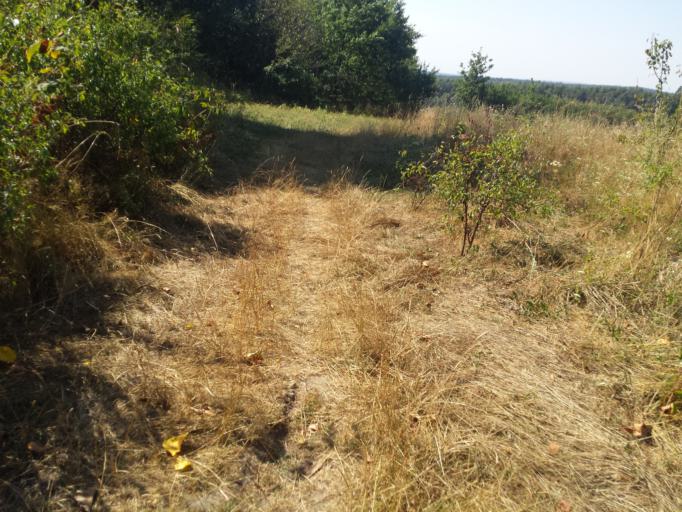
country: PL
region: Swietokrzyskie
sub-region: Powiat kielecki
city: Daleszyce
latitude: 50.8030
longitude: 20.7703
